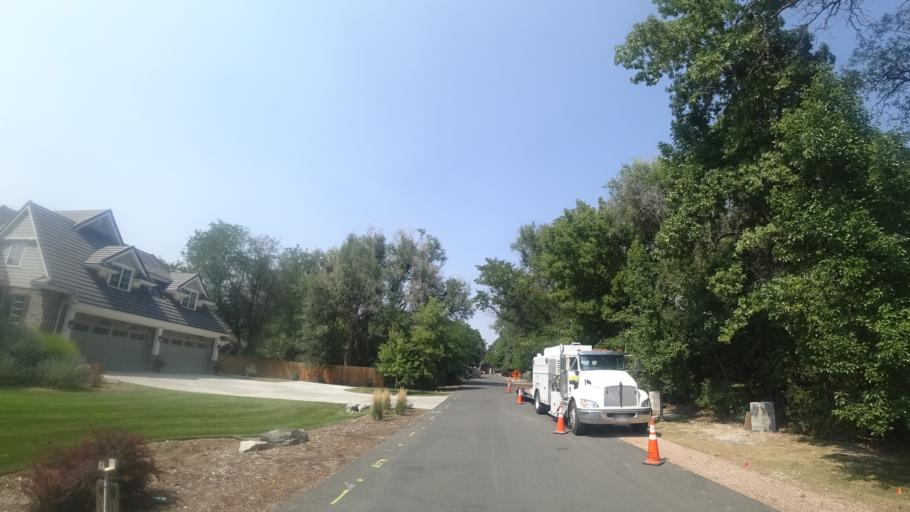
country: US
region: Colorado
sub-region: Arapahoe County
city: Cherry Hills Village
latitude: 39.6297
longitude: -104.9739
